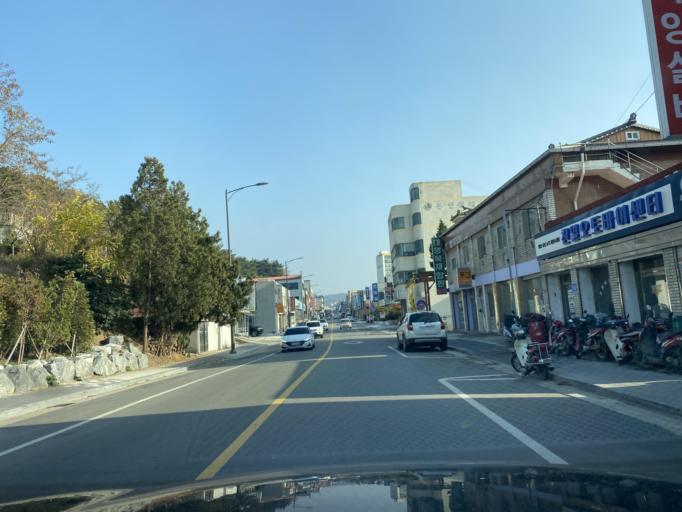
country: KR
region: Chungcheongnam-do
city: Yesan
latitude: 36.6807
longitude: 126.8341
